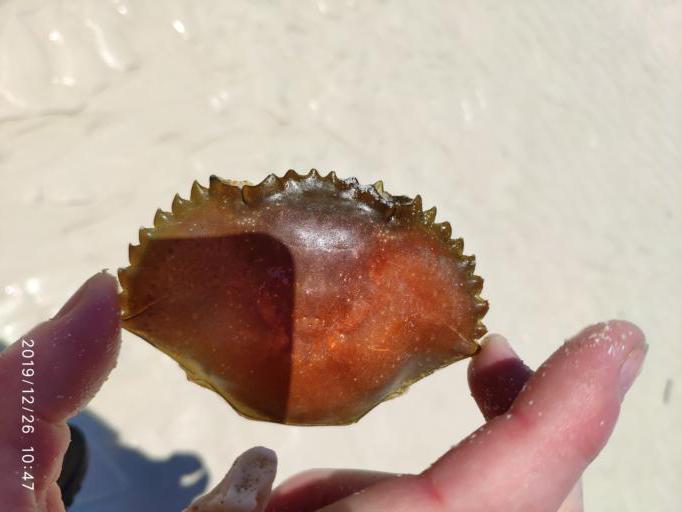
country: MG
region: Diana
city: Hell-Ville
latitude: -13.6012
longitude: 47.8211
